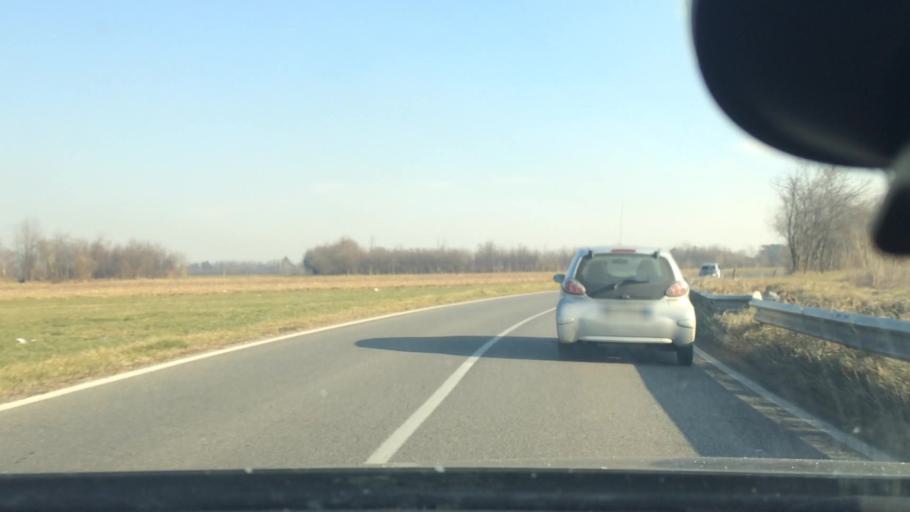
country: IT
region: Lombardy
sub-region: Citta metropolitana di Milano
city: Arluno
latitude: 45.5127
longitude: 8.9223
